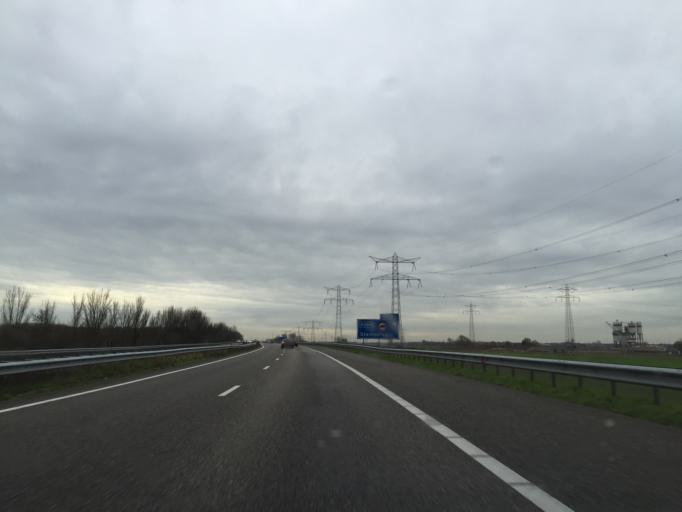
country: NL
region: North Brabant
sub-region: Gemeente Moerdijk
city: Klundert
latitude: 51.6144
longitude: 4.5045
